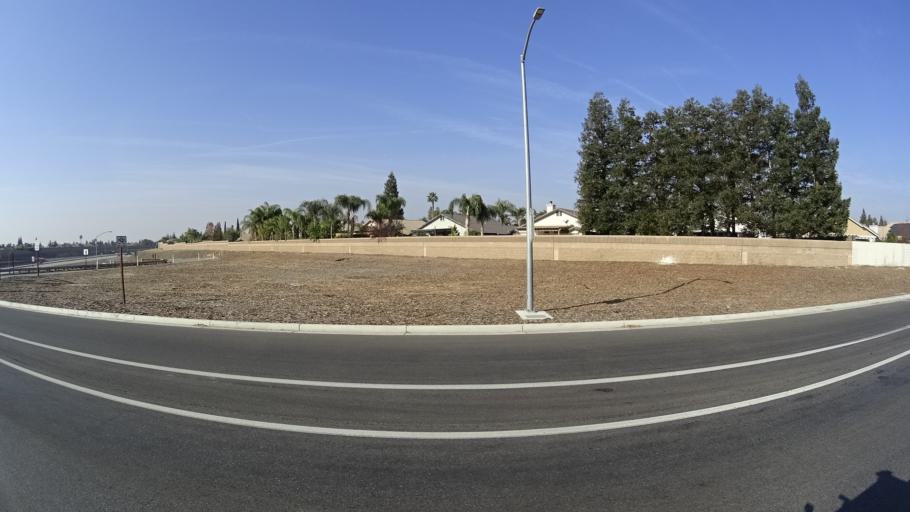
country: US
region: California
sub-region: Kern County
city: Greenacres
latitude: 35.3633
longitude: -119.1157
